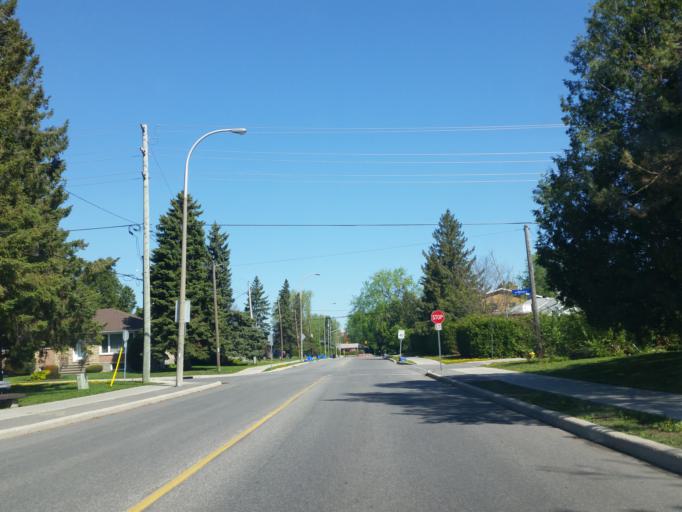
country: CA
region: Ontario
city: Ottawa
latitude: 45.3427
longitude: -75.7457
